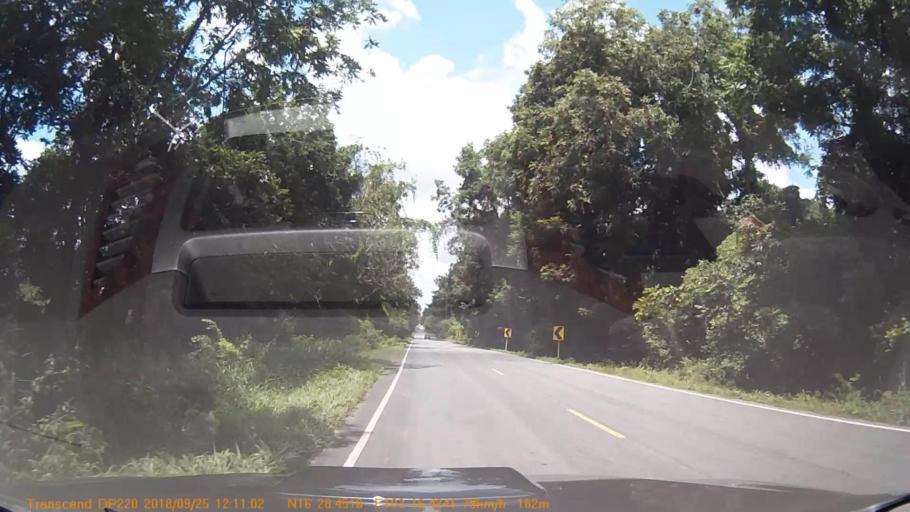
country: TH
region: Kalasin
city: Yang Talat
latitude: 16.4744
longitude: 103.2736
